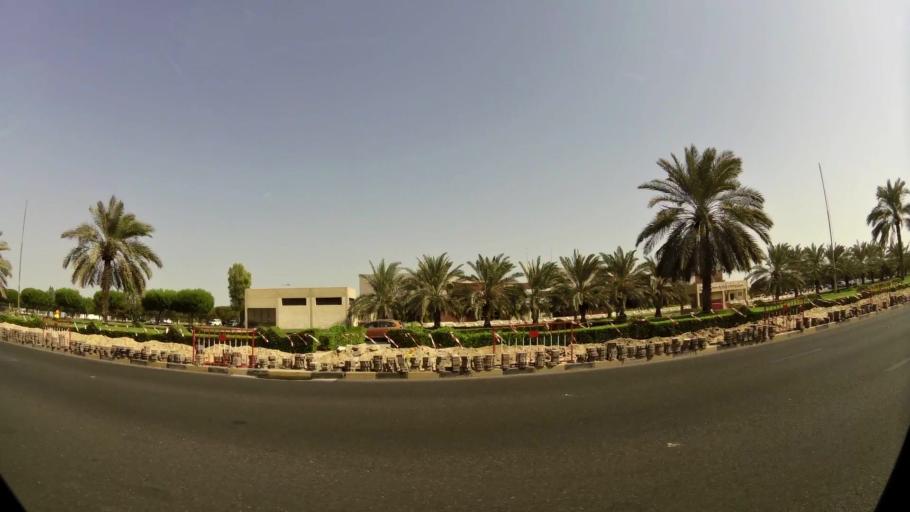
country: KW
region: Al Asimah
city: Ad Dasmah
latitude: 29.3633
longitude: 48.0226
